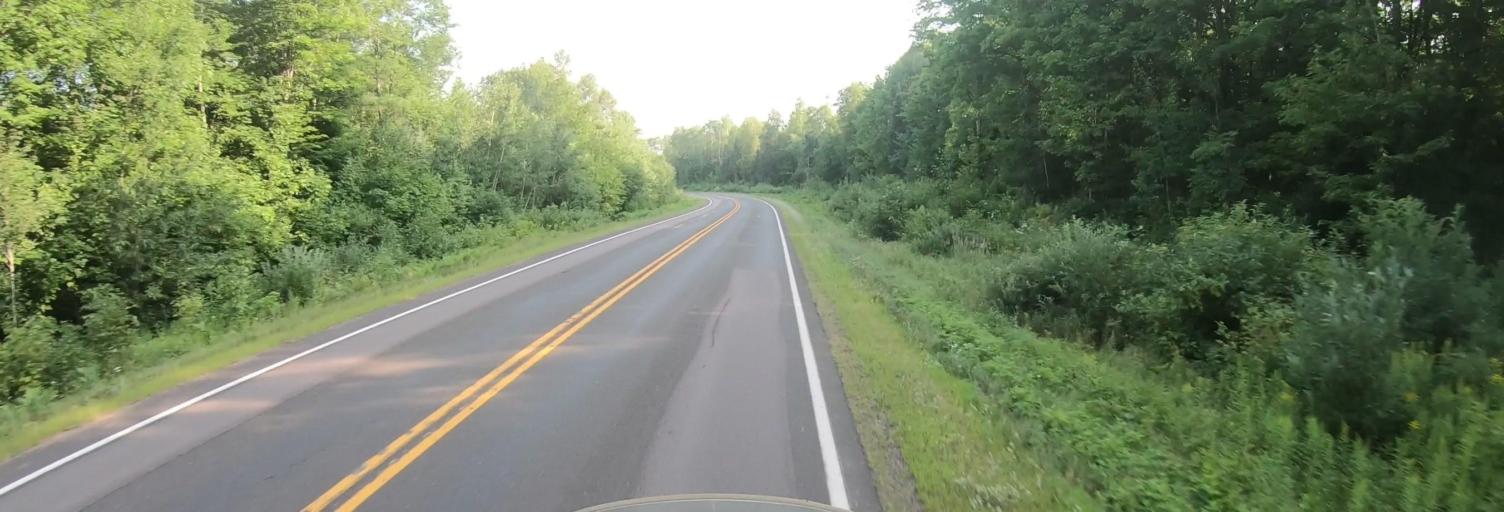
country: US
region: Wisconsin
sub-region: Ashland County
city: Ashland
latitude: 46.2616
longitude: -90.8427
